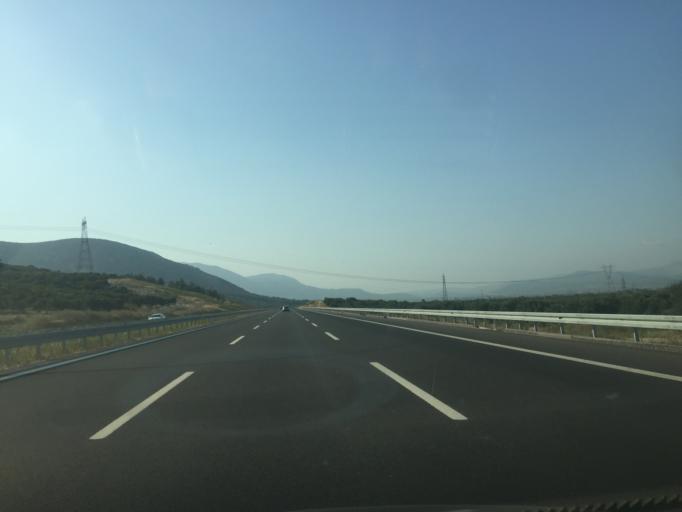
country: TR
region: Manisa
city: Kirkagac
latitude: 39.0567
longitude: 27.7275
